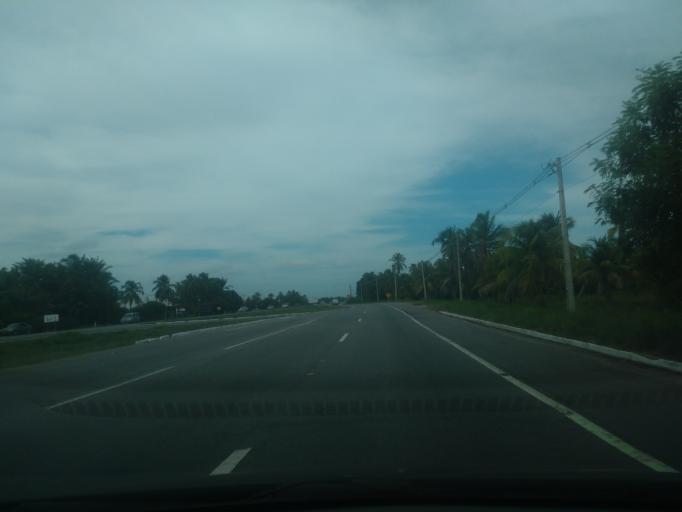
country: BR
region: Alagoas
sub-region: Maceio
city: Maceio
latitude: -9.7040
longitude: -35.8065
